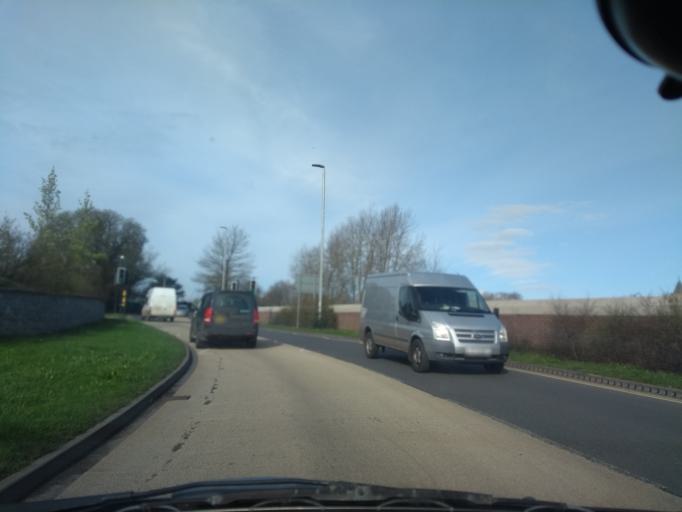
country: GB
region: England
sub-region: Somerset
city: Taunton
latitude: 51.0241
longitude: -3.1132
